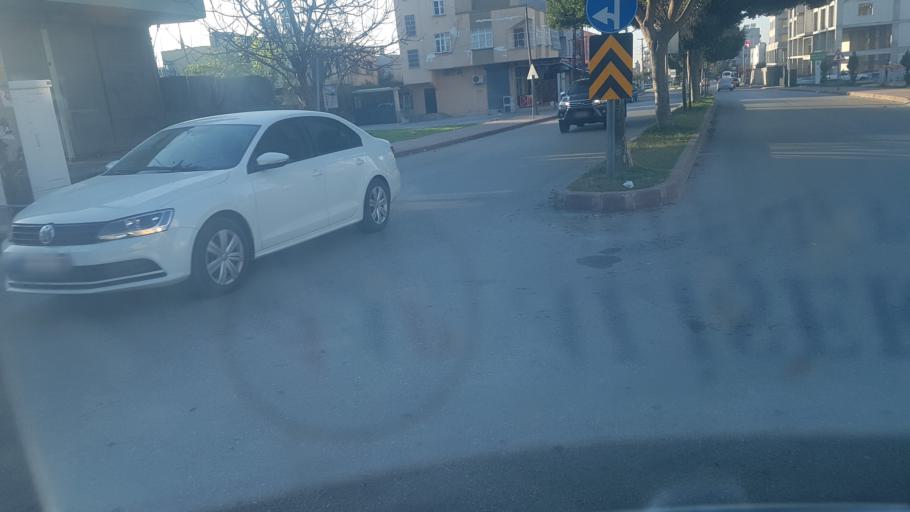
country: TR
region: Adana
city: Seyhan
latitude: 37.0227
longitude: 35.2721
